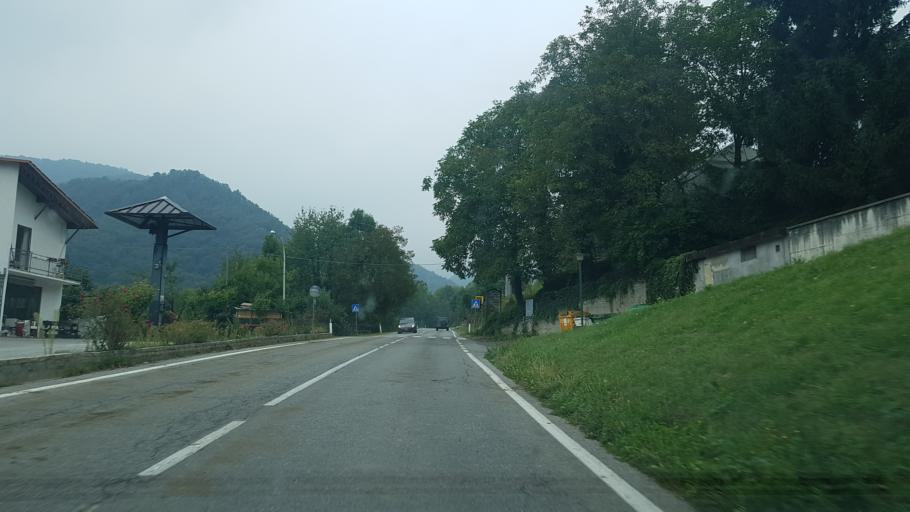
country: IT
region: Piedmont
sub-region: Provincia di Cuneo
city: Frabosa Sottana
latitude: 44.3164
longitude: 7.8036
